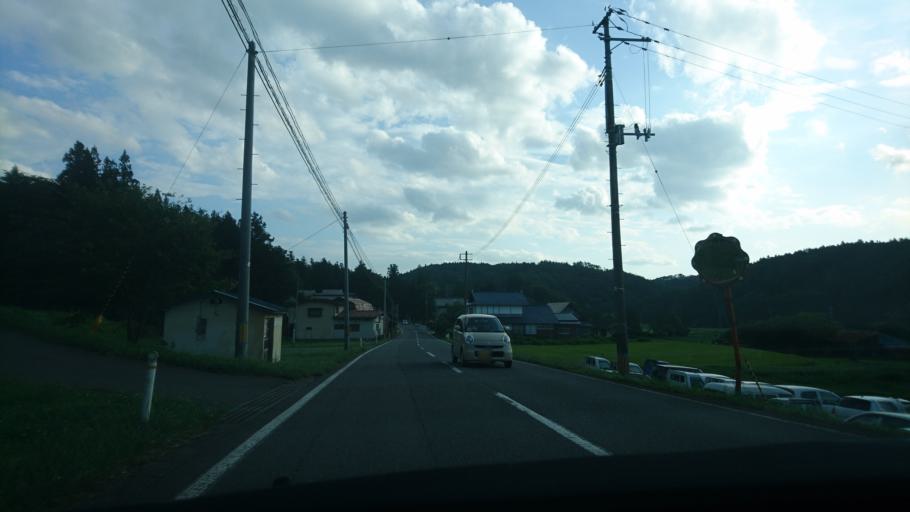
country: JP
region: Iwate
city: Ichinoseki
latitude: 39.0208
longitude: 141.2904
